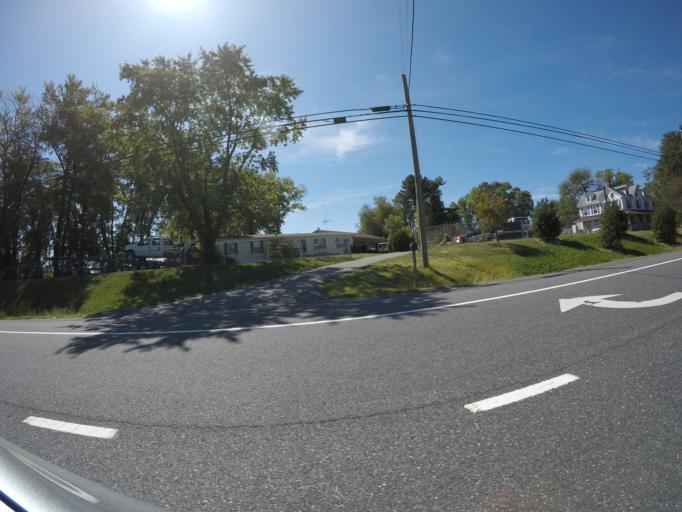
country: US
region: Maryland
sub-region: Harford County
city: Perryman
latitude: 39.4891
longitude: -76.1994
